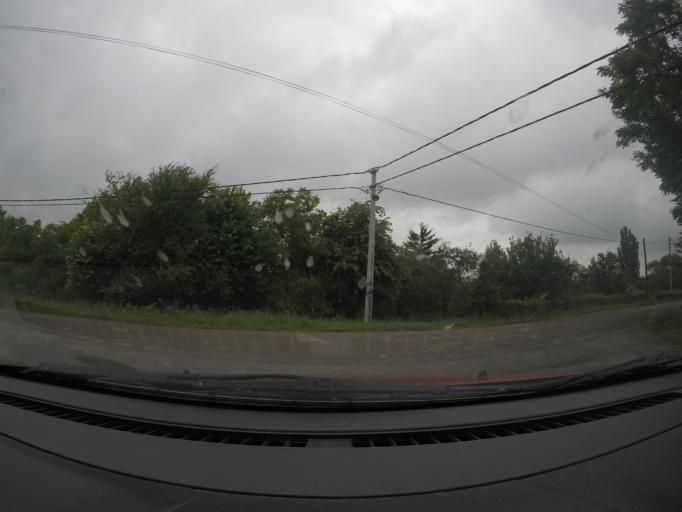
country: RS
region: Central Serbia
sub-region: Belgrade
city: Sopot
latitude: 44.5596
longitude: 20.5188
